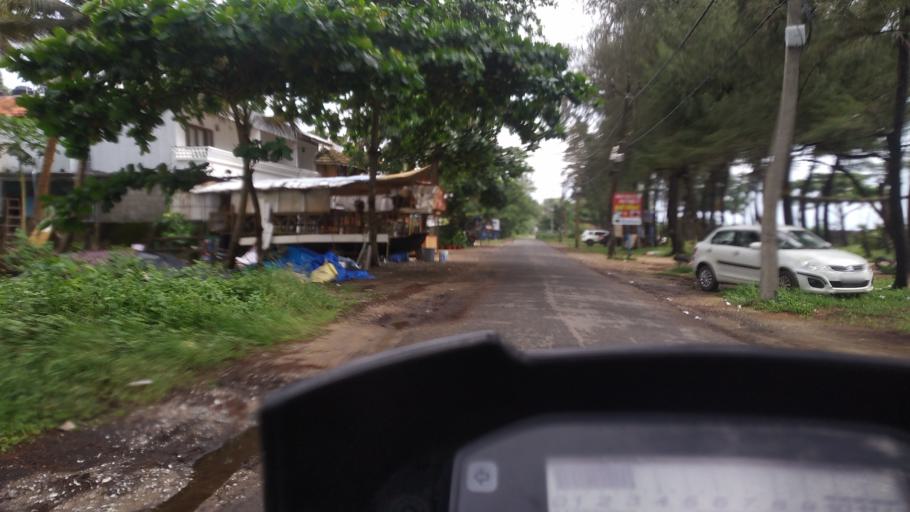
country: IN
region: Kerala
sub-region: Thrissur District
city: Kodungallur
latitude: 10.1522
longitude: 76.1750
